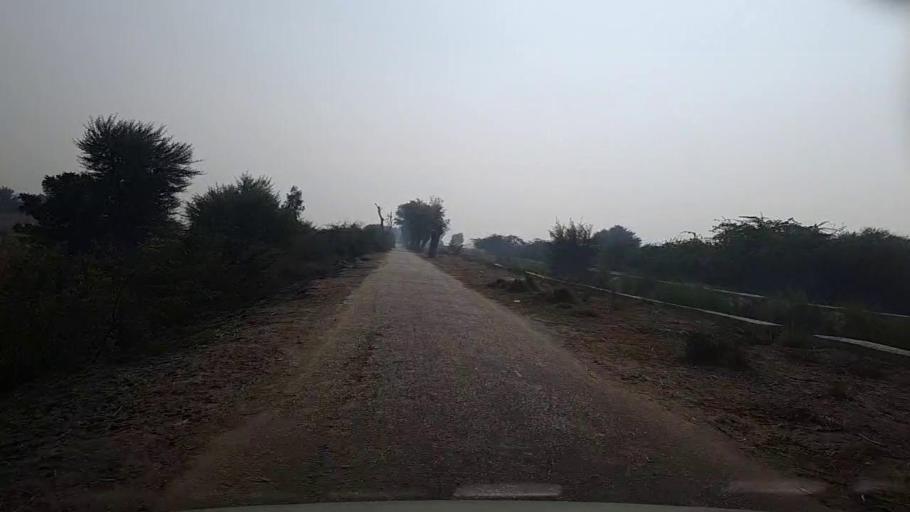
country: PK
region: Sindh
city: Setharja Old
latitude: 27.1039
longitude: 68.5077
